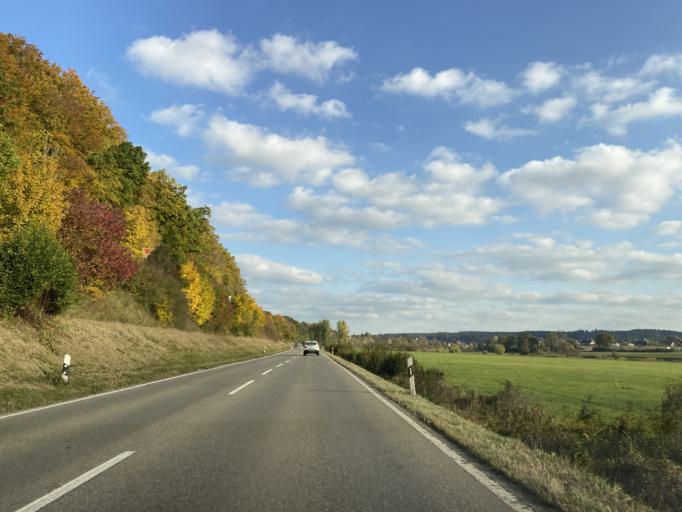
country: DE
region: Baden-Wuerttemberg
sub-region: Tuebingen Region
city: Sigmaringendorf
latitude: 48.0750
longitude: 9.2463
